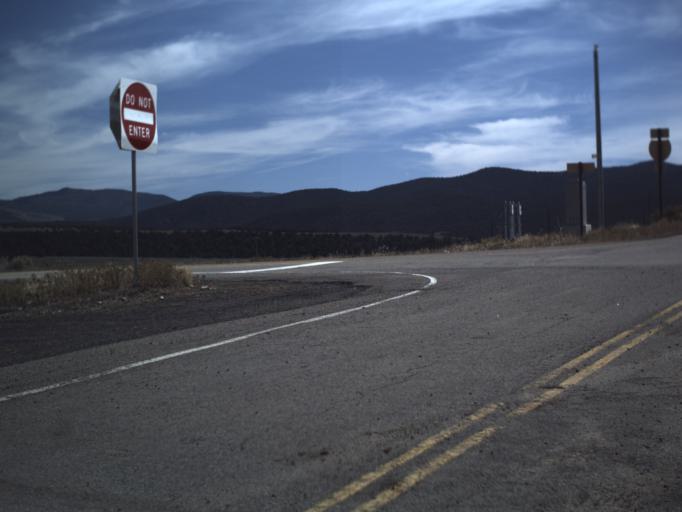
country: US
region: Utah
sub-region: Beaver County
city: Beaver
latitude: 38.1311
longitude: -112.6289
